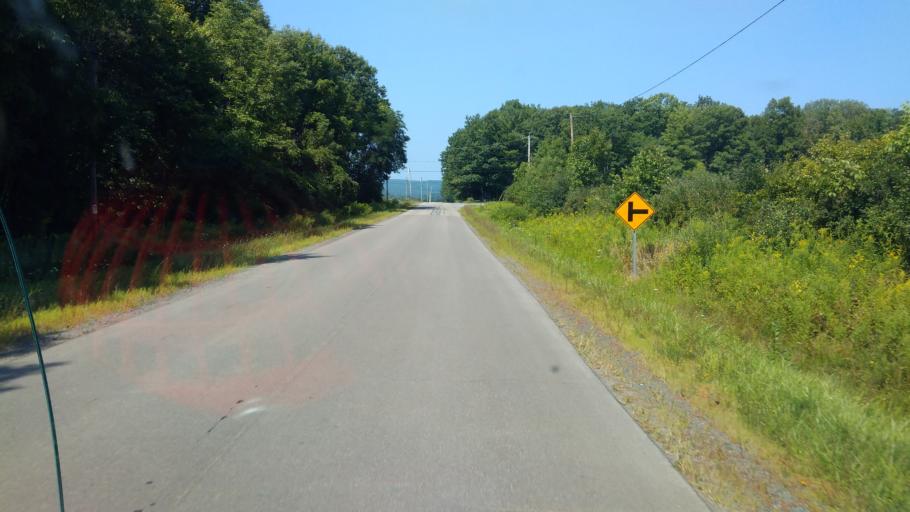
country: US
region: New York
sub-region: Allegany County
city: Belmont
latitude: 42.3120
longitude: -78.0656
